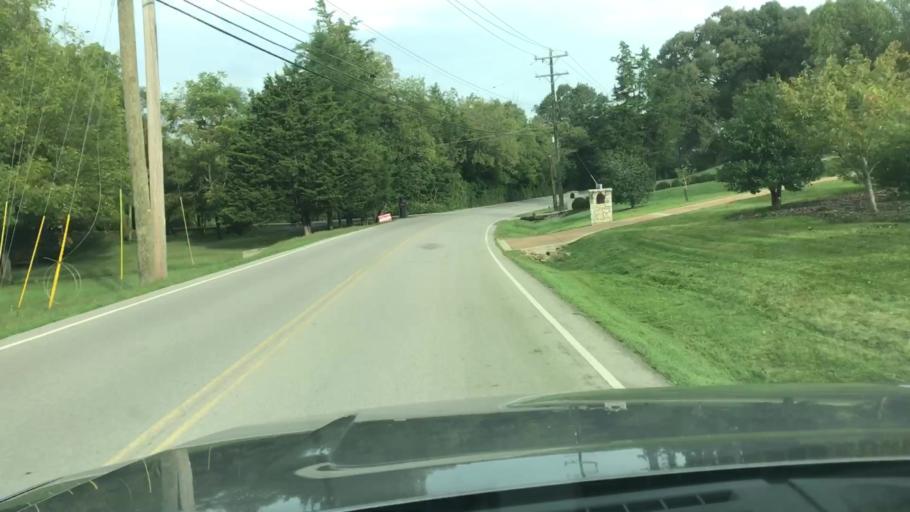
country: US
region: Tennessee
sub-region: Davidson County
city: Forest Hills
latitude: 36.0719
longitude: -86.8312
